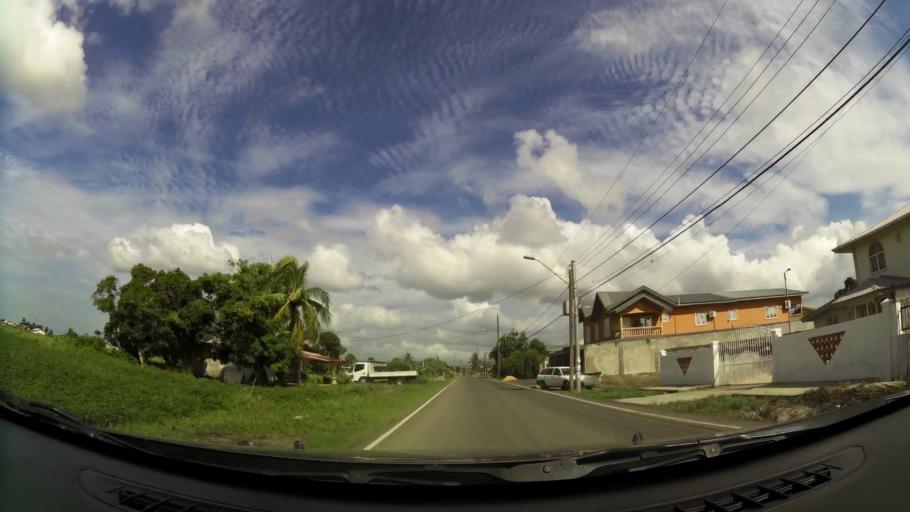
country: TT
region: Chaguanas
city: Chaguanas
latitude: 10.5405
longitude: -61.3891
